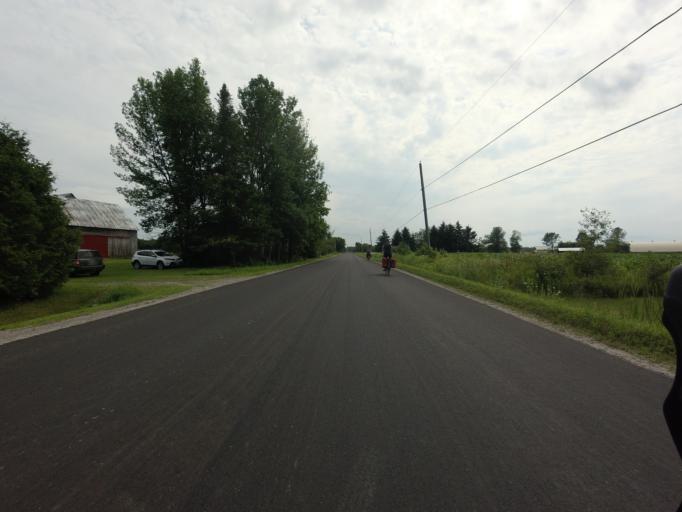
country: CA
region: Ontario
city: Bells Corners
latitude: 45.0678
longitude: -75.6024
